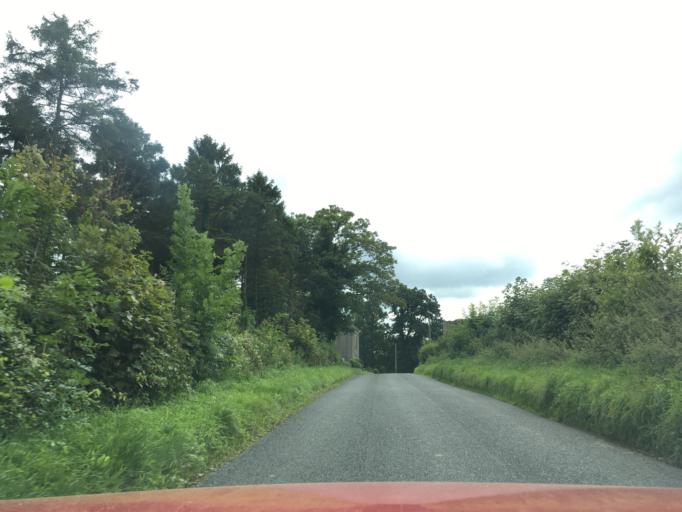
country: GB
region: England
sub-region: South Gloucestershire
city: Charfield
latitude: 51.6360
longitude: -2.4293
